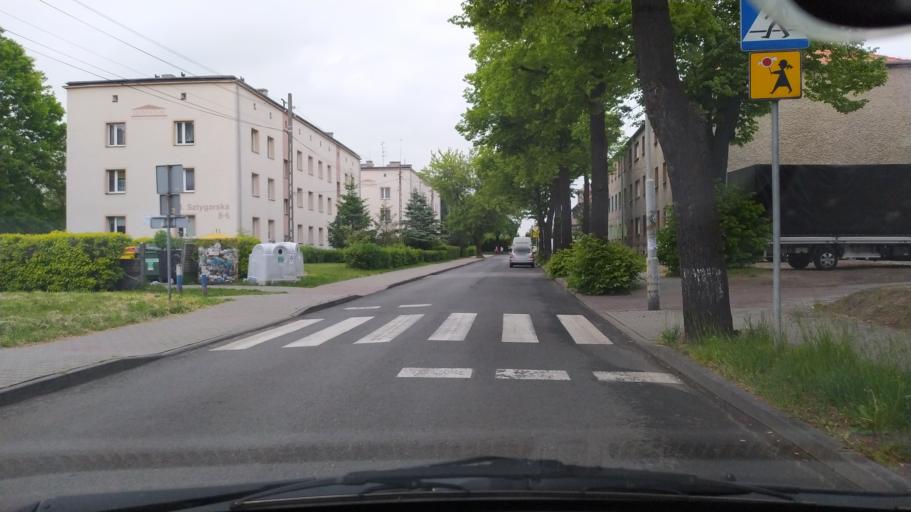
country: PL
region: Silesian Voivodeship
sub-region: Powiat gliwicki
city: Przyszowice
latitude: 50.2916
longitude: 18.7401
